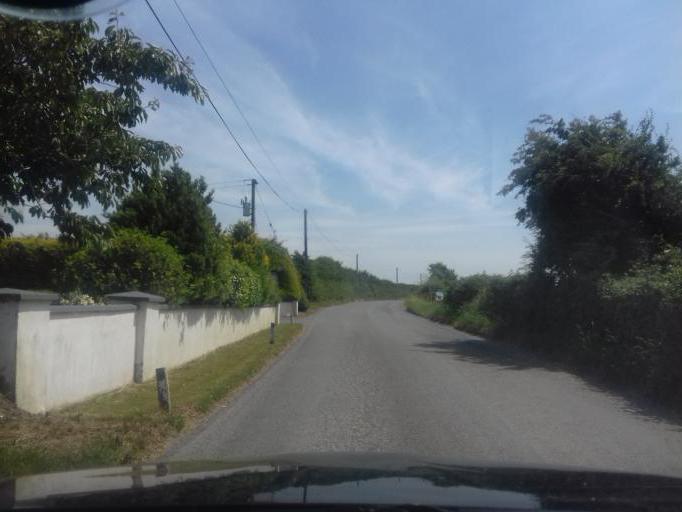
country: IE
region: Leinster
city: Lusk
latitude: 53.5386
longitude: -6.1908
